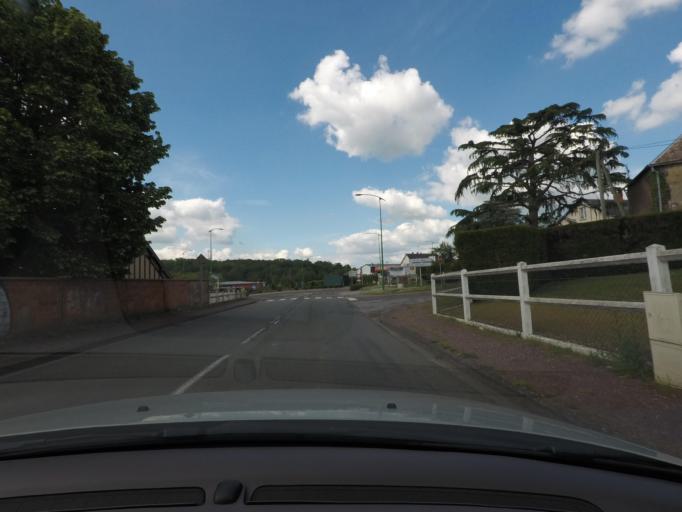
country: FR
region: Haute-Normandie
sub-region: Departement de l'Eure
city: Damville
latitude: 48.8707
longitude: 1.0792
